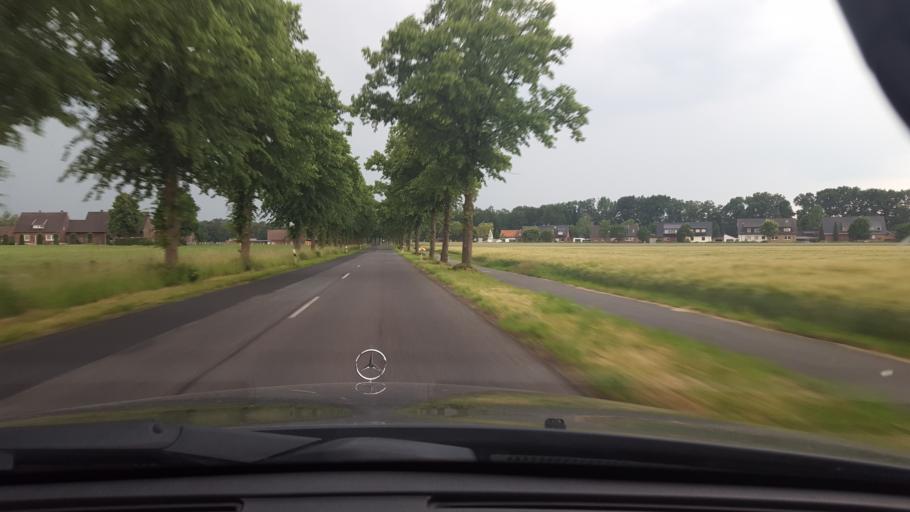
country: DE
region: North Rhine-Westphalia
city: Olfen
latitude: 51.7083
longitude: 7.3592
